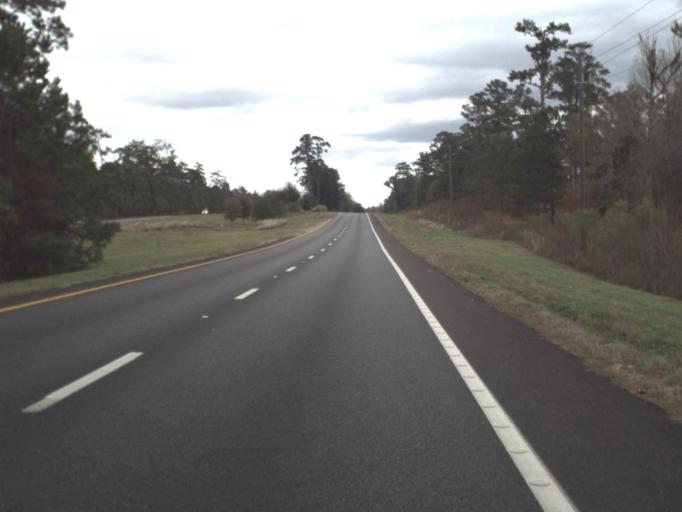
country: US
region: Florida
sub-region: Leon County
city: Tallahassee
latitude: 30.6027
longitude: -84.1817
